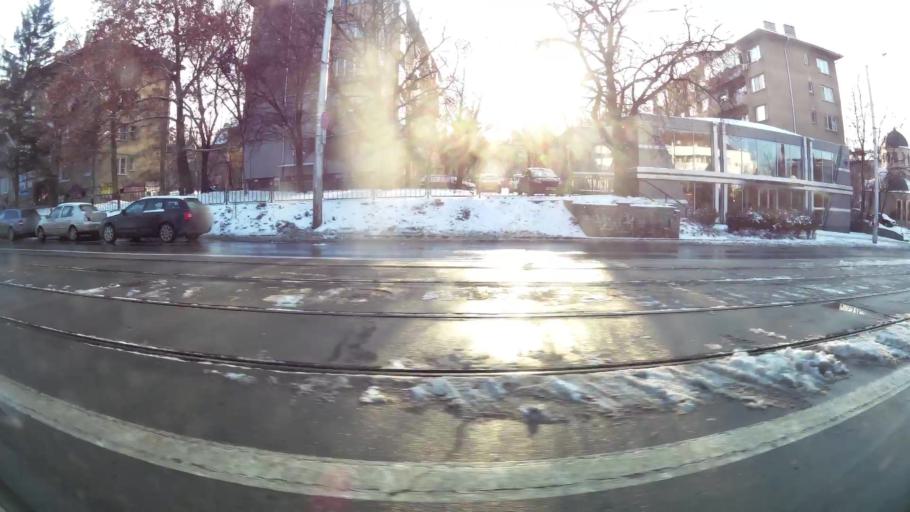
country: BG
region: Sofia-Capital
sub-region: Stolichna Obshtina
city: Sofia
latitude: 42.6850
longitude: 23.3515
